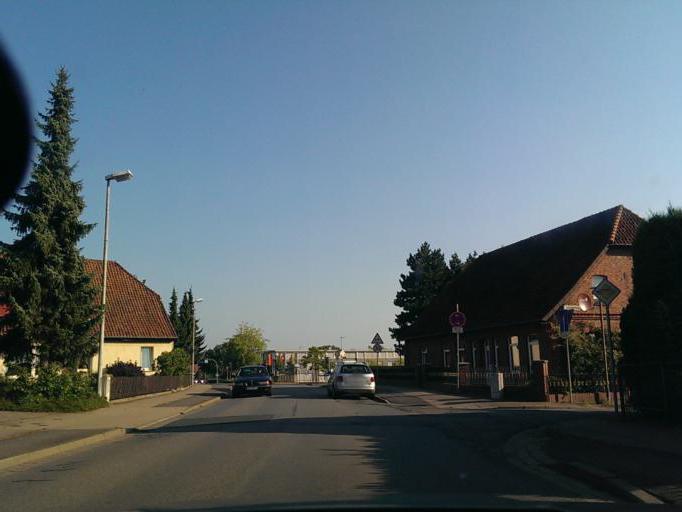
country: DE
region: Lower Saxony
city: Elze
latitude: 52.5486
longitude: 9.7325
